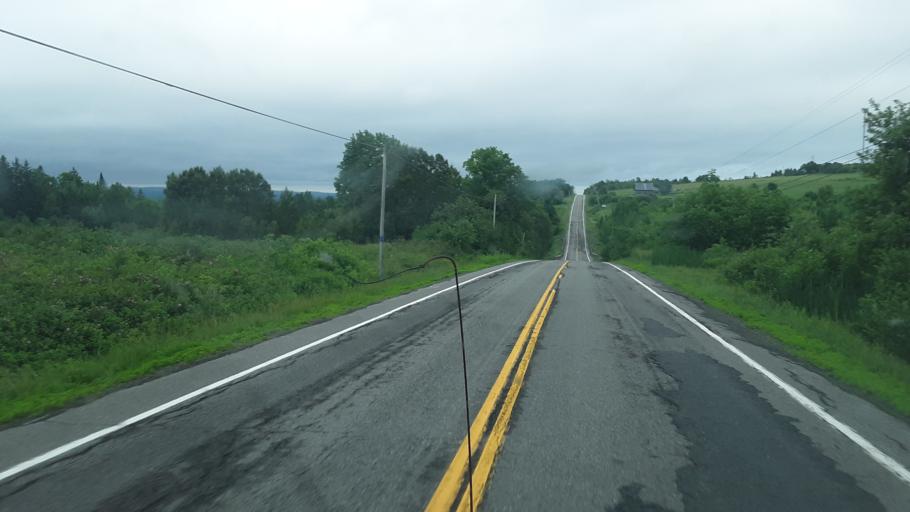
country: US
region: Maine
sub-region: Penobscot County
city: Patten
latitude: 46.0383
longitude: -68.4442
